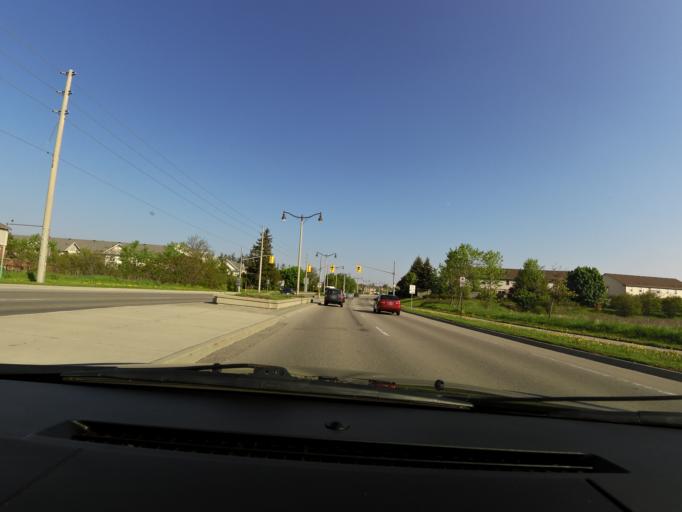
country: CA
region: Ontario
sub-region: Wellington County
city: Guelph
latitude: 43.5024
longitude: -80.1918
